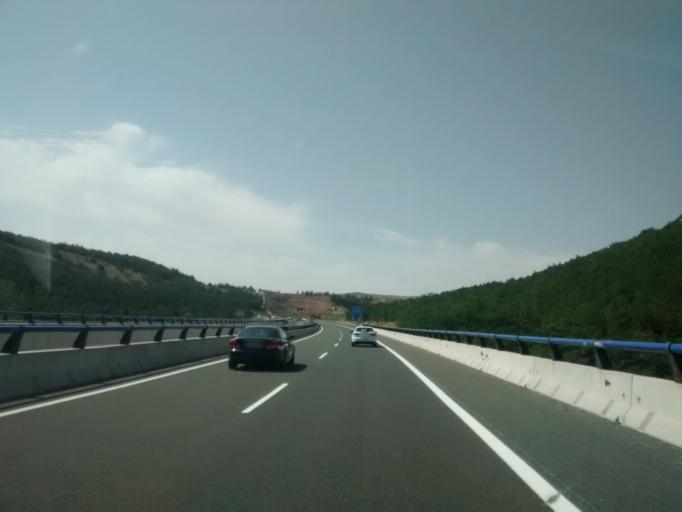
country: ES
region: Castille and Leon
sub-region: Provincia de Palencia
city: Alar del Rey
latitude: 42.6942
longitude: -4.2983
